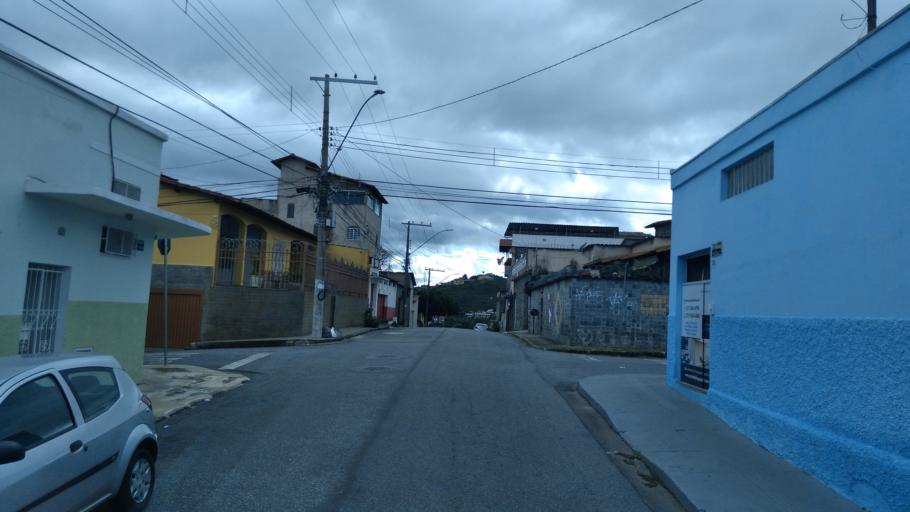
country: BR
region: Minas Gerais
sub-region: Belo Horizonte
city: Belo Horizonte
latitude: -19.9225
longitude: -43.9057
